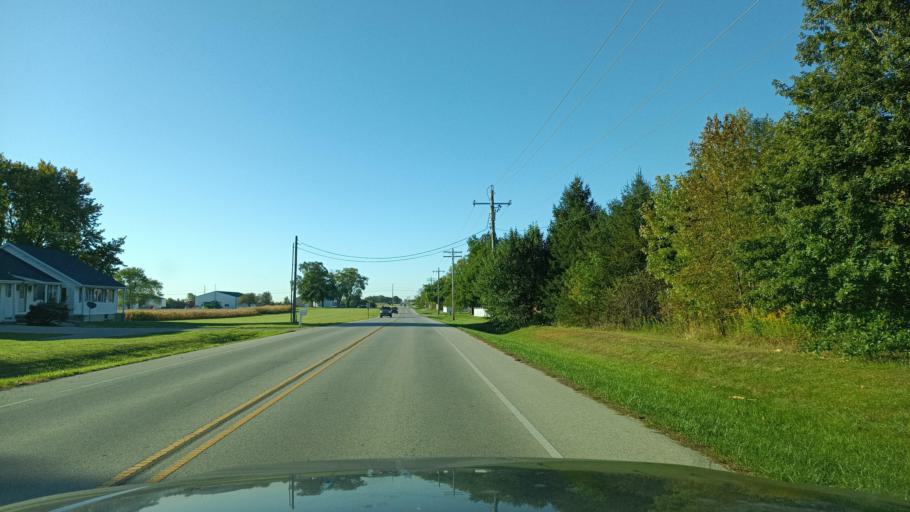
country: US
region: Illinois
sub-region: Champaign County
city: Savoy
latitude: 40.0613
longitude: -88.2384
